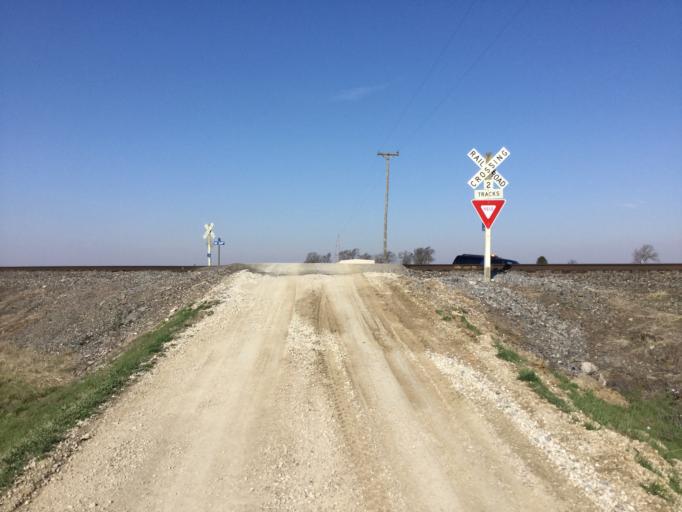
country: US
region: Kansas
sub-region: Anderson County
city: Garnett
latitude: 38.2417
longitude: -95.2812
